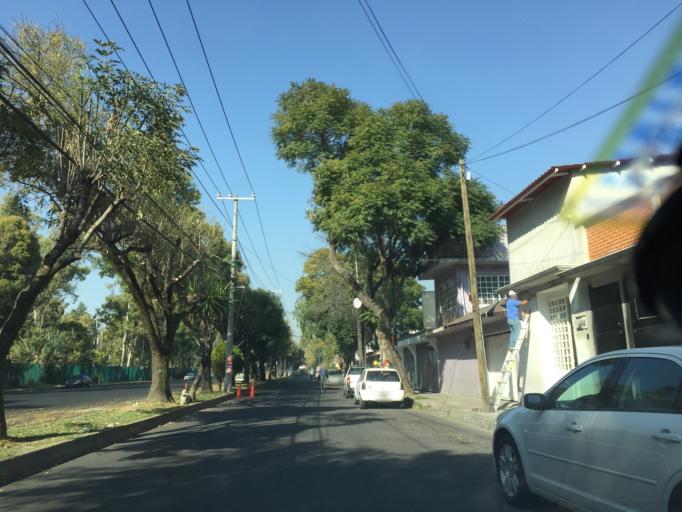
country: MX
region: Mexico
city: Vista Hermosa
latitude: 19.5012
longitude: -99.2078
